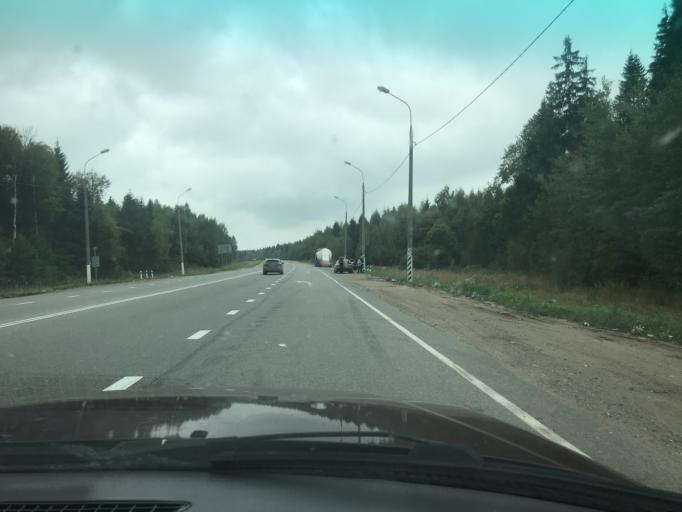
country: RU
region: Kaluga
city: Maloyaroslavets
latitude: 54.9794
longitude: 36.4860
